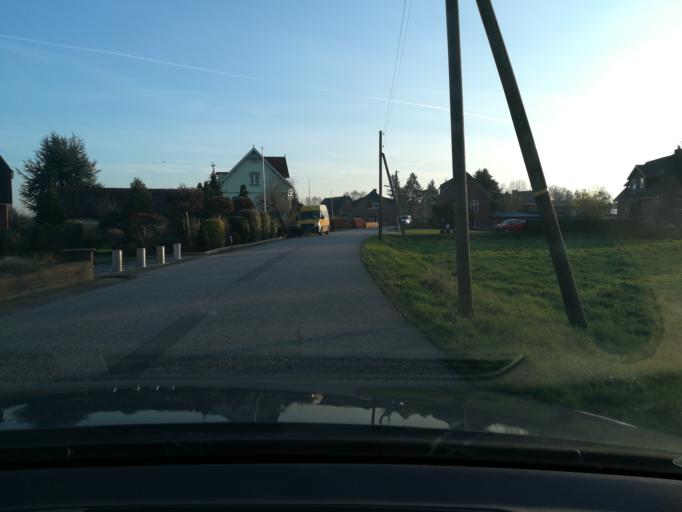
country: DE
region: Lower Saxony
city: Drage
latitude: 53.4256
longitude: 10.2057
